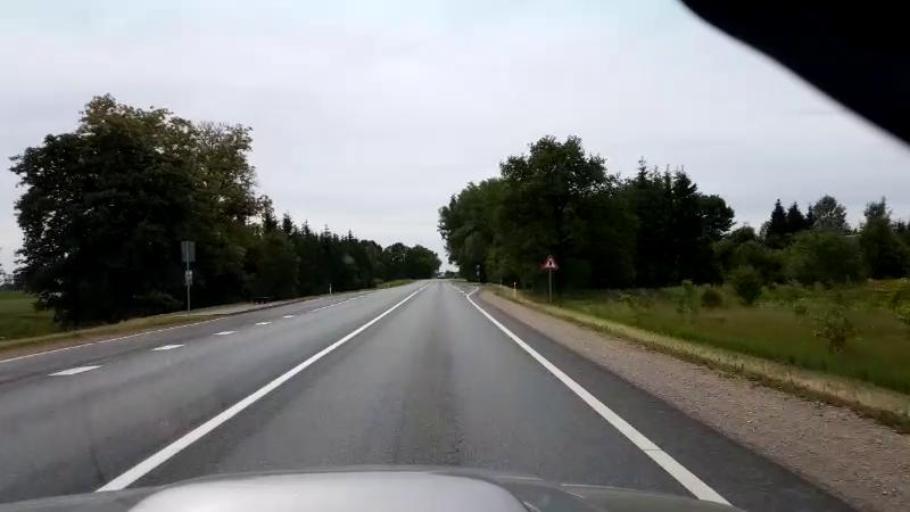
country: LV
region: Lecava
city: Iecava
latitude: 56.5514
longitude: 24.1733
